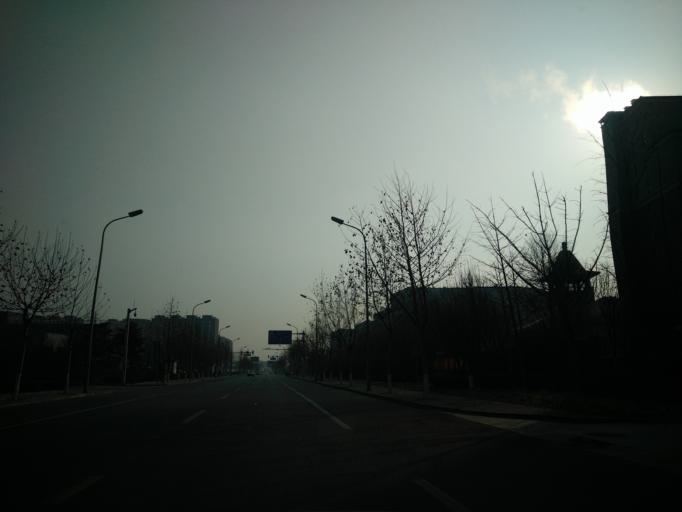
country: CN
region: Beijing
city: Yinghai
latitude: 39.7141
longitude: 116.3967
